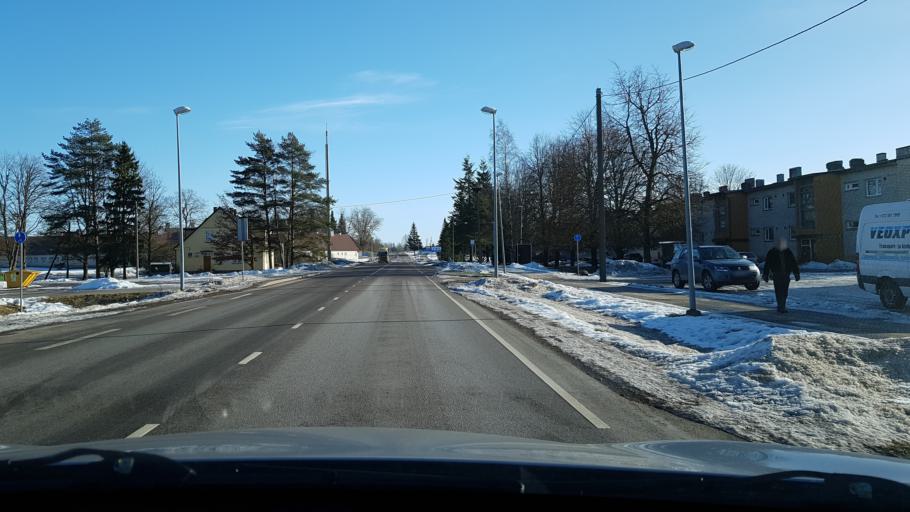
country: EE
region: Viljandimaa
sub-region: Vohma linn
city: Vohma
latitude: 58.6321
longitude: 25.7238
